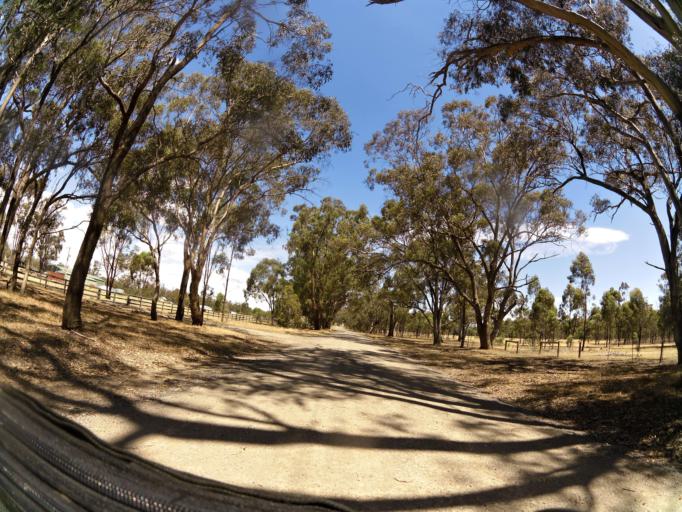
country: AU
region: Victoria
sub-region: Campaspe
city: Kyabram
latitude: -36.8132
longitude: 145.0784
